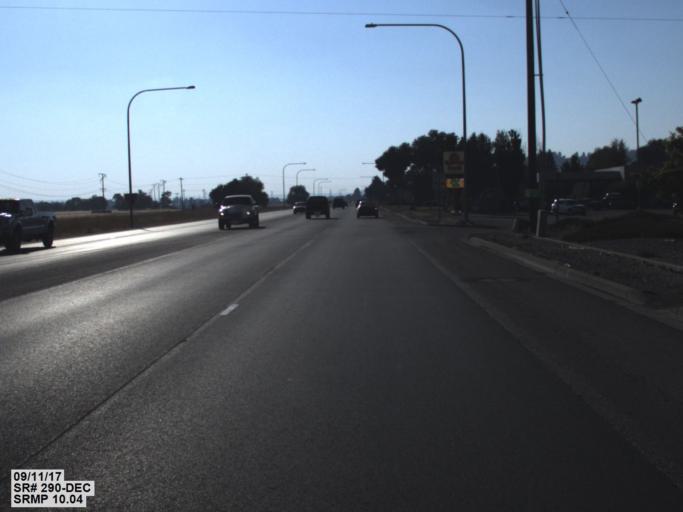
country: US
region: Washington
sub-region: Spokane County
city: Trentwood
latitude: 47.6951
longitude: -117.2072
